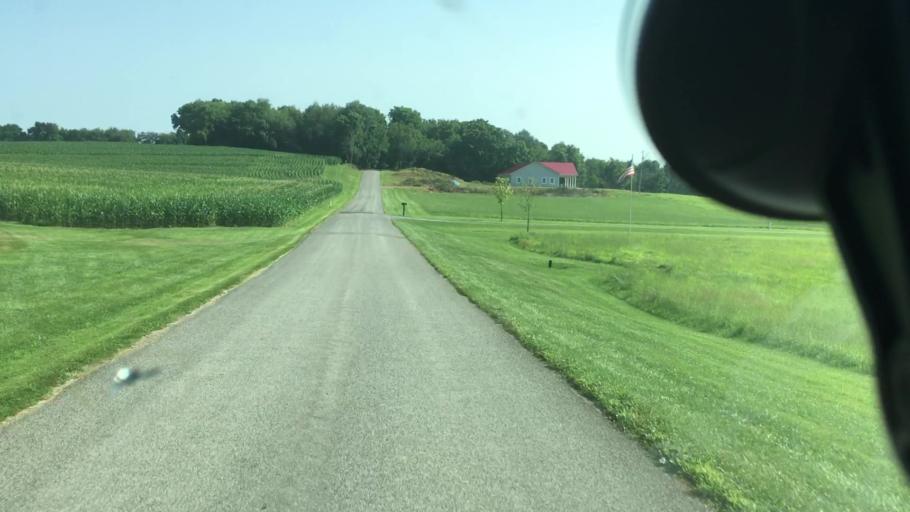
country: US
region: Pennsylvania
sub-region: Butler County
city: Slippery Rock
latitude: 41.0509
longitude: -80.1740
